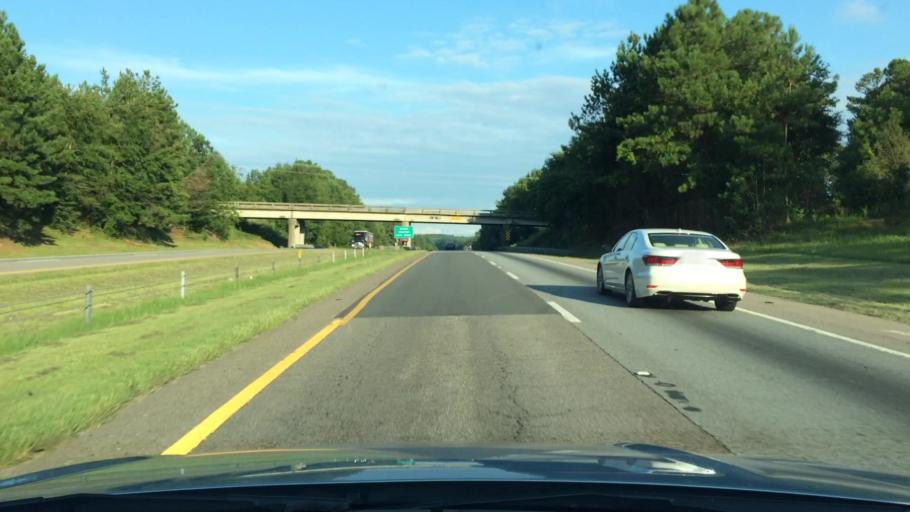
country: US
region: South Carolina
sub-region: Newberry County
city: Prosperity
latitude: 34.2531
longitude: -81.4883
